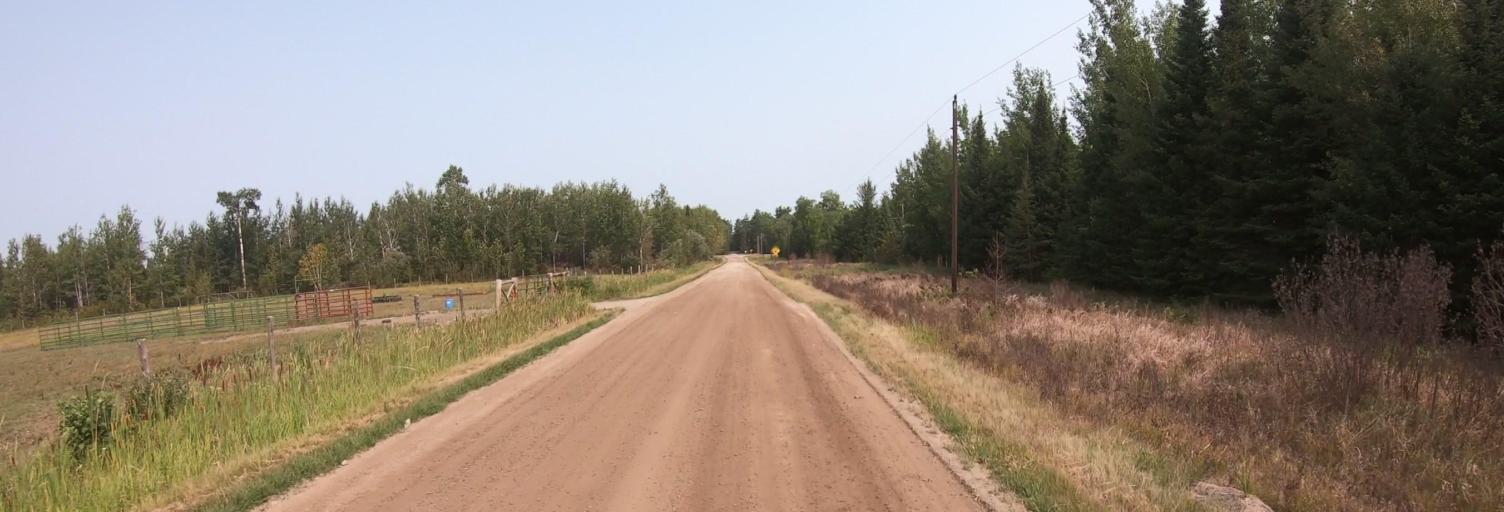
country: US
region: Minnesota
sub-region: Saint Louis County
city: Mountain Iron
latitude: 47.8644
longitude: -92.7400
